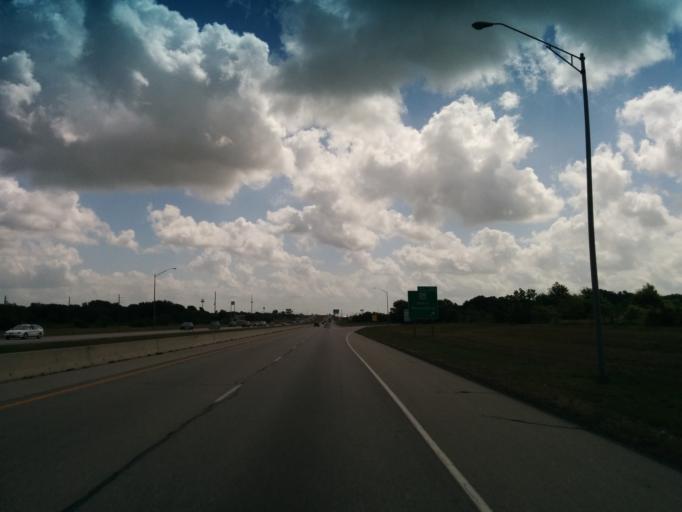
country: US
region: Texas
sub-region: Austin County
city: Sealy
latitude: 29.7614
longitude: -96.1627
